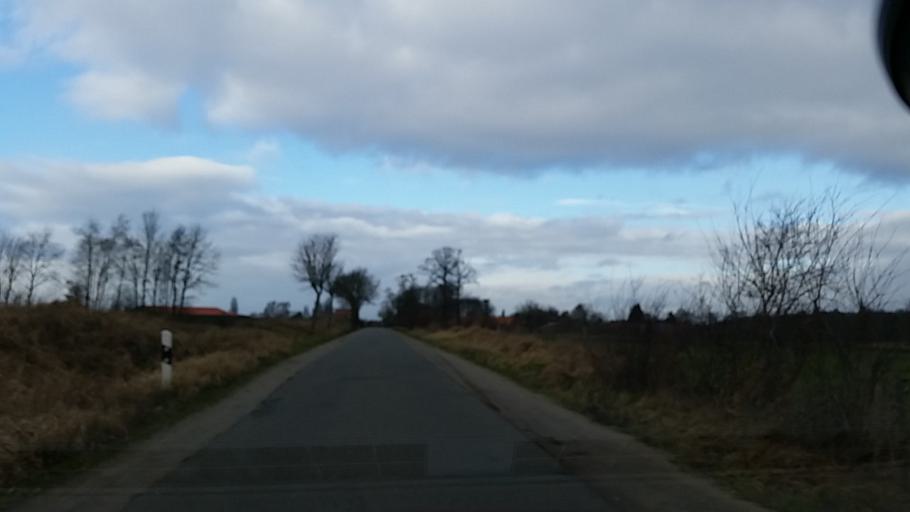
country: DE
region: Lower Saxony
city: Wieren
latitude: 52.8779
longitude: 10.6554
